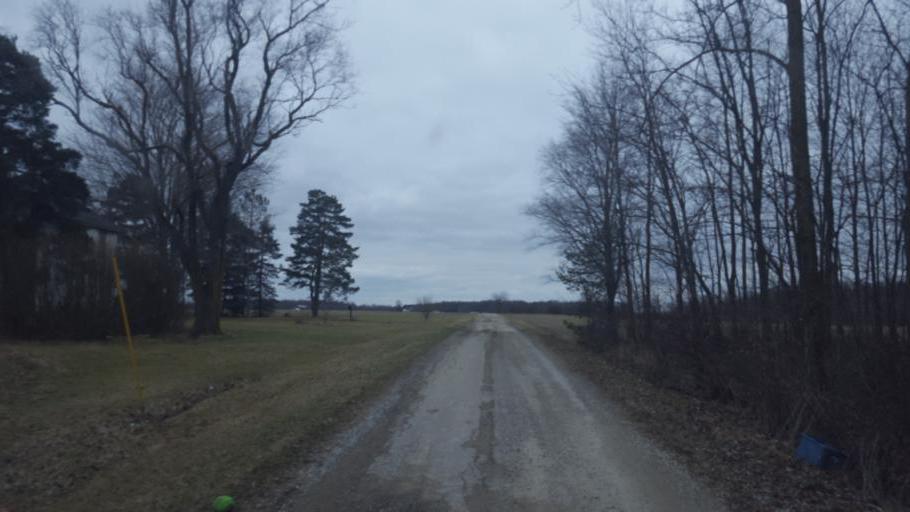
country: US
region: Ohio
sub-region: Morrow County
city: Mount Gilead
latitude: 40.6165
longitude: -82.7146
